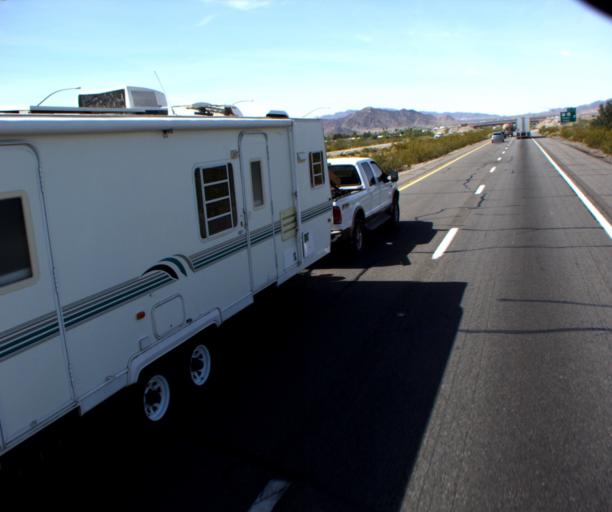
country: US
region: Arizona
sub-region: La Paz County
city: Quartzsite
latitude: 33.6667
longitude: -114.1913
